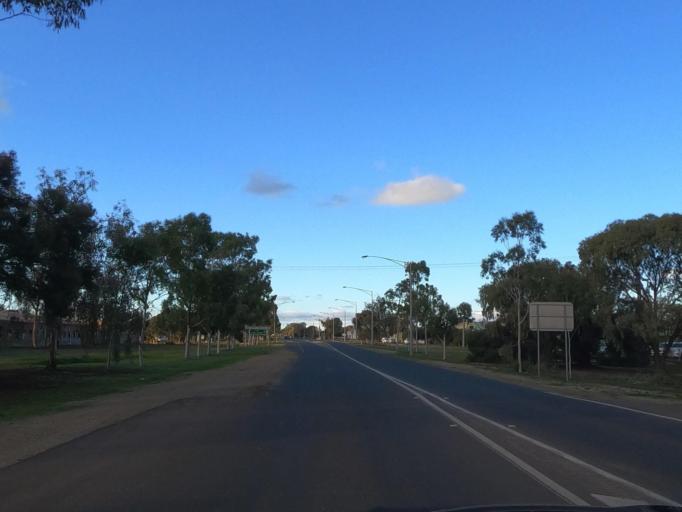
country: AU
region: Victoria
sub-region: Swan Hill
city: Swan Hill
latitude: -35.3428
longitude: 143.5321
